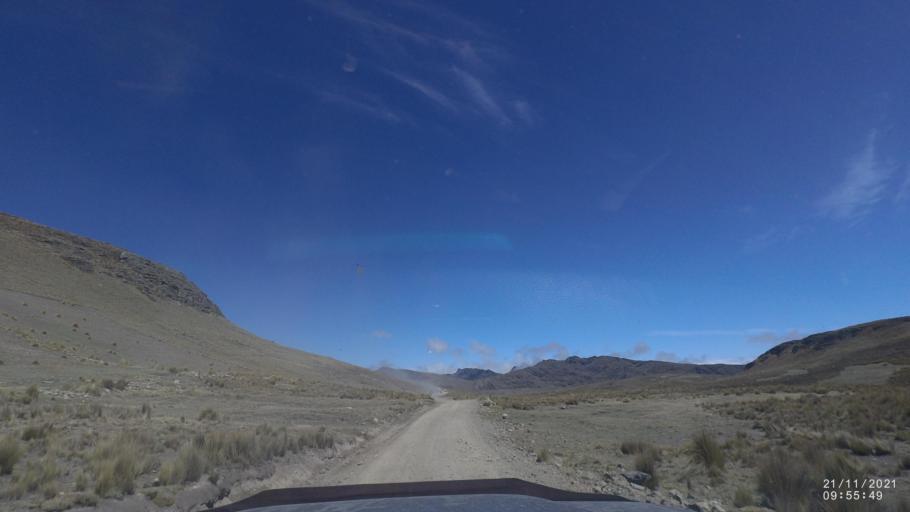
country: BO
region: Cochabamba
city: Cochabamba
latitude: -17.0448
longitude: -66.2641
